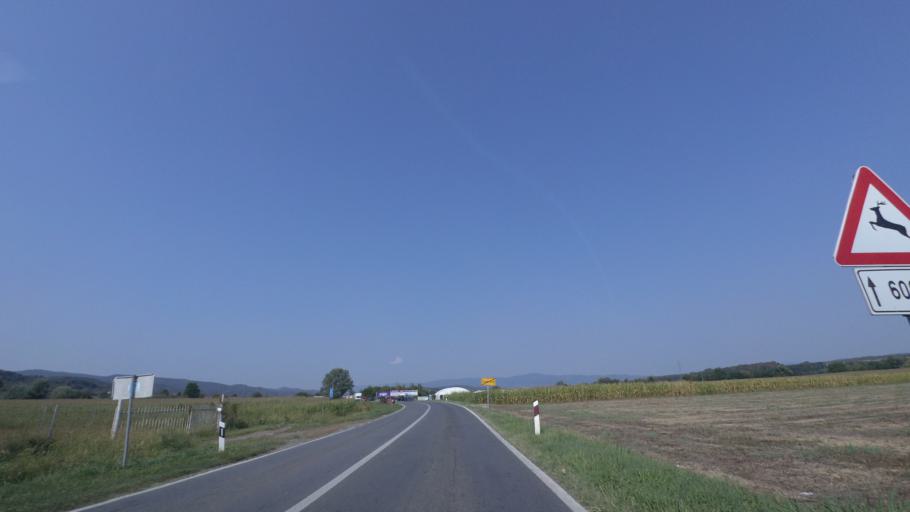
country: HR
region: Pozesko-Slavonska
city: Pozega
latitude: 45.3276
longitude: 17.6219
